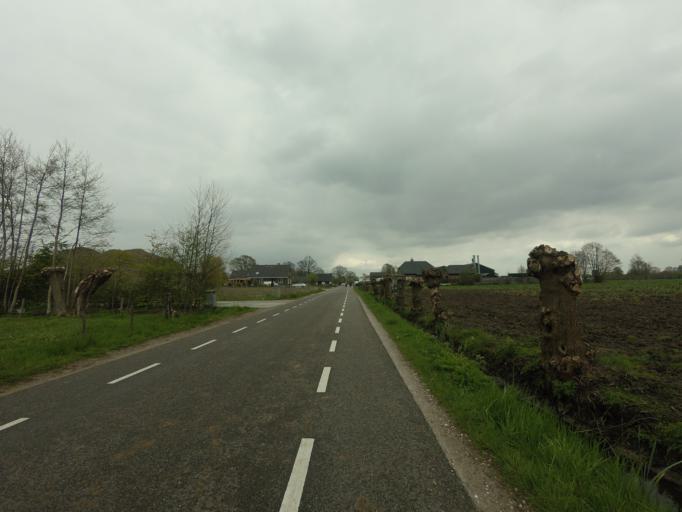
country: NL
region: Gelderland
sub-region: Gemeente Ede
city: Ederveen
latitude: 52.0678
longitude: 5.5697
